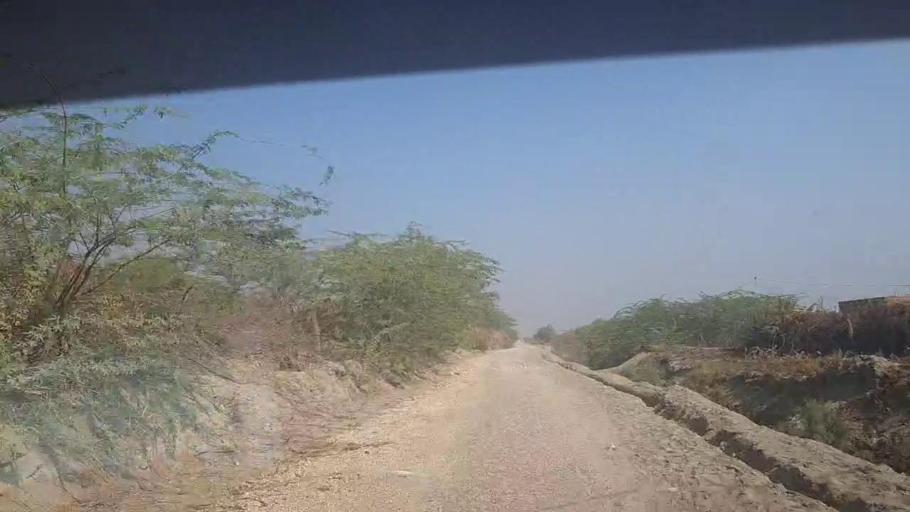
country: PK
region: Sindh
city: Khairpur
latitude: 27.4589
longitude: 68.7272
